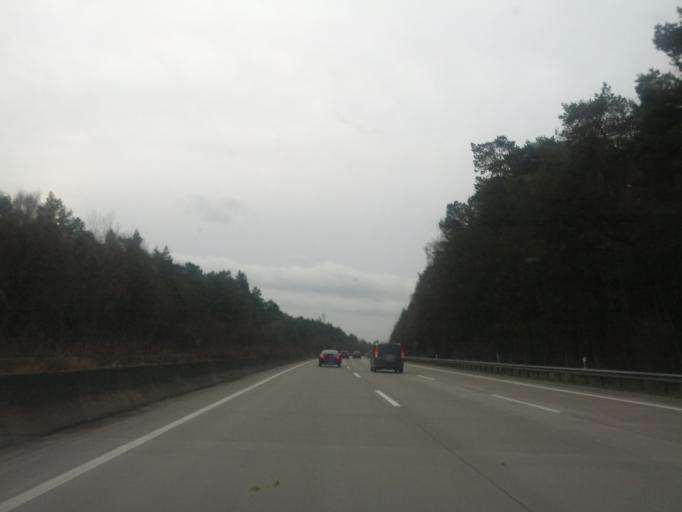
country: DE
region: Lower Saxony
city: Garlstorf
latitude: 53.2603
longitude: 10.0880
